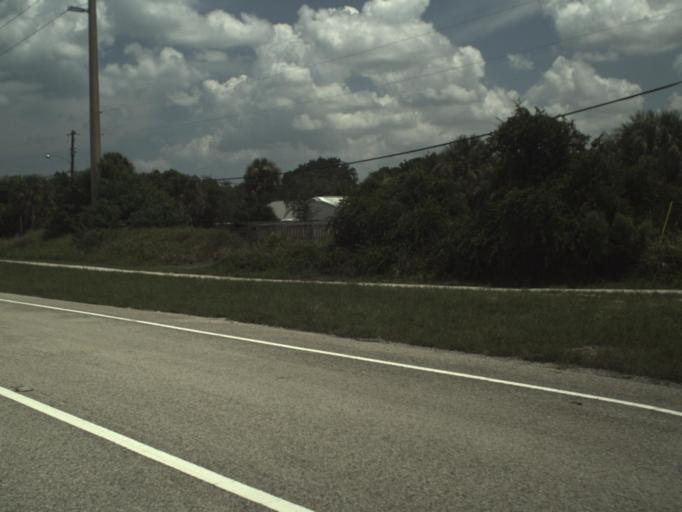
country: US
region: Florida
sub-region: Martin County
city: Hobe Sound
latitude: 27.0497
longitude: -80.1267
